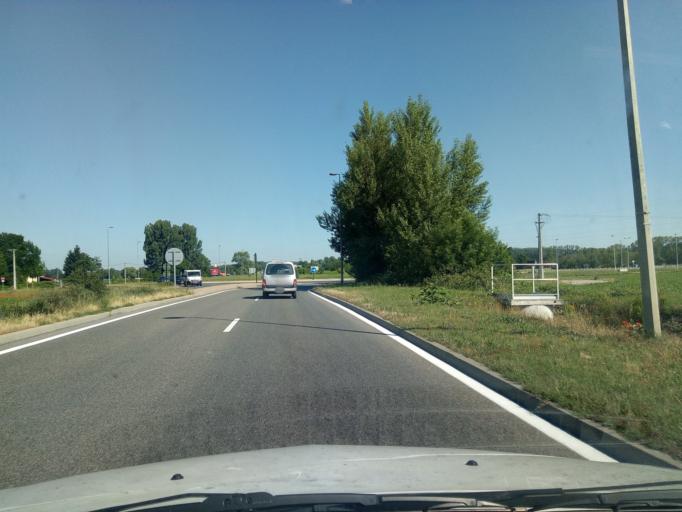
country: FR
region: Rhone-Alpes
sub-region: Departement de l'Isere
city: Saint-Alban-de-Roche
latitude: 45.6027
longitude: 5.2339
